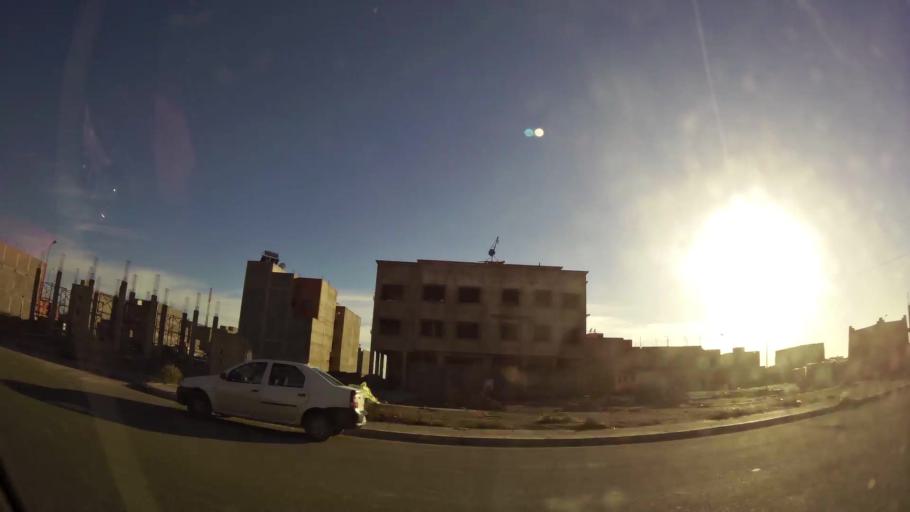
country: MA
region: Marrakech-Tensift-Al Haouz
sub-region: Marrakech
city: Marrakesh
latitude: 31.7629
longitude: -8.1126
